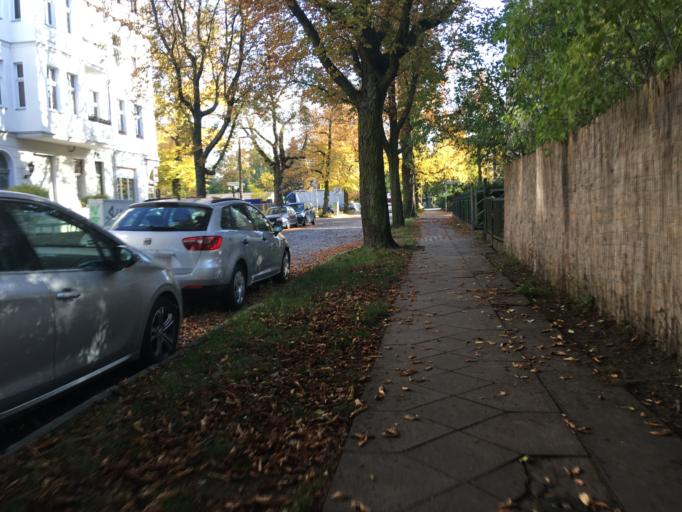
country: DE
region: Berlin
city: Niederschonhausen
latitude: 52.5885
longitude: 13.4118
